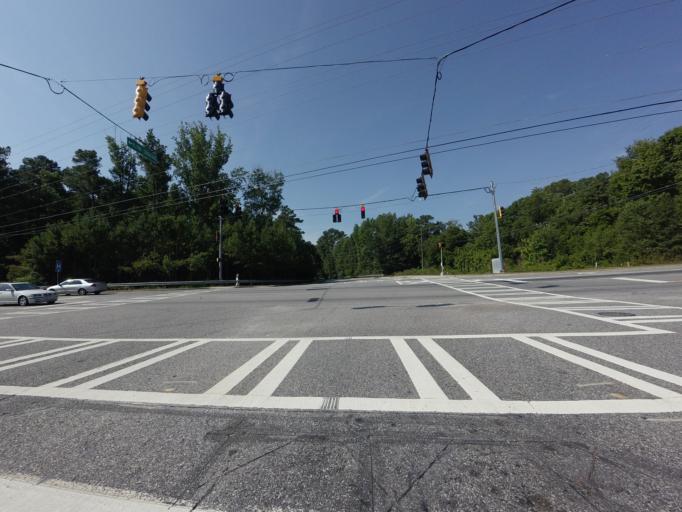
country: US
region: Georgia
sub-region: Fulton County
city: Johns Creek
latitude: 34.0907
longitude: -84.2056
